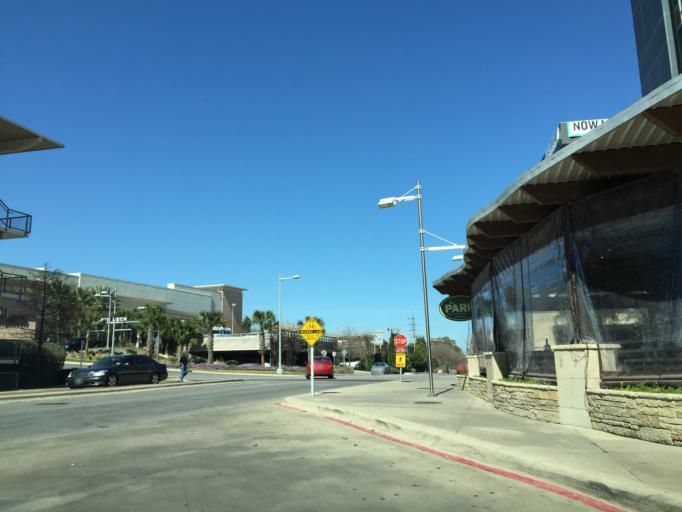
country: US
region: Texas
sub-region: Travis County
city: Wells Branch
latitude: 30.4029
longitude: -97.7239
